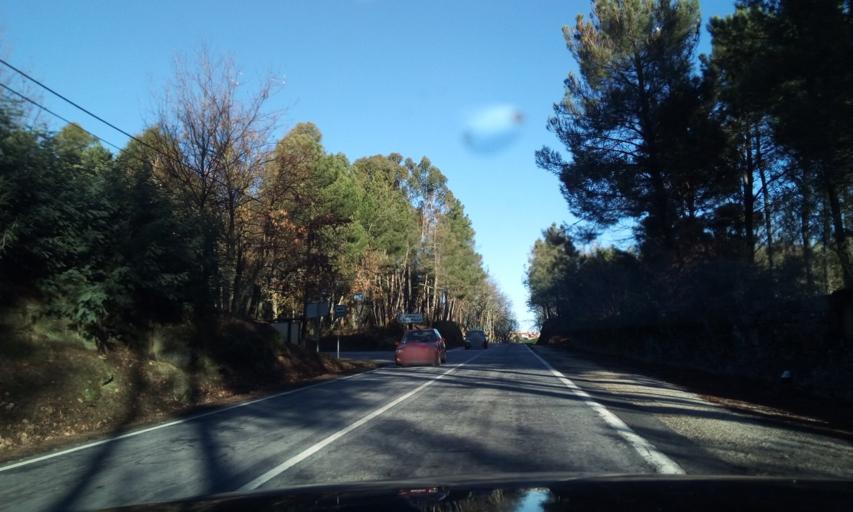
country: PT
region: Guarda
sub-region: Seia
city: Seia
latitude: 40.4417
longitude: -7.7092
